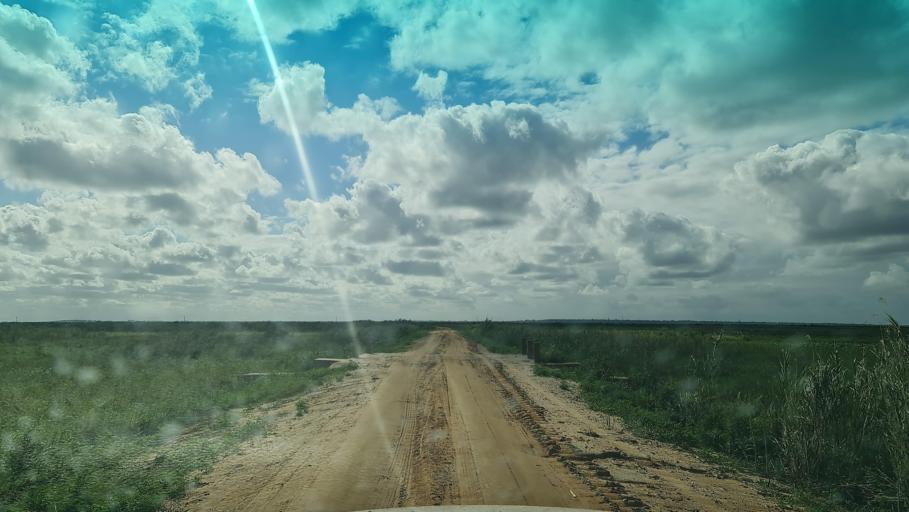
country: MZ
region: Maputo
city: Manhica
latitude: -25.4342
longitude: 32.8676
